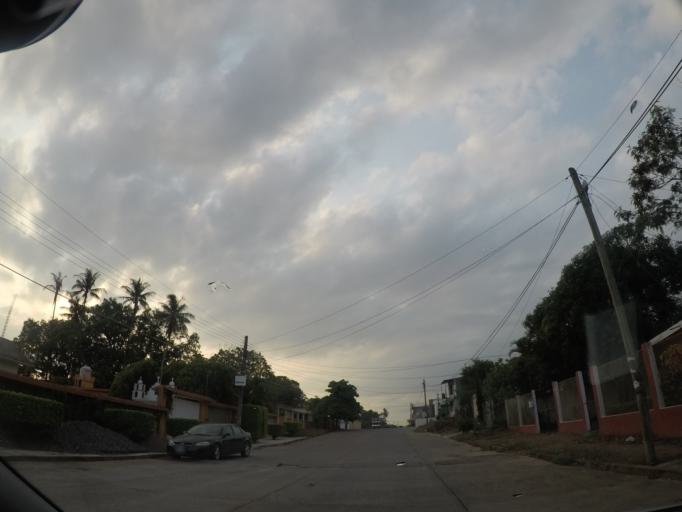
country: MX
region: Oaxaca
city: Matias Romero
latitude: 16.8733
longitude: -95.0385
